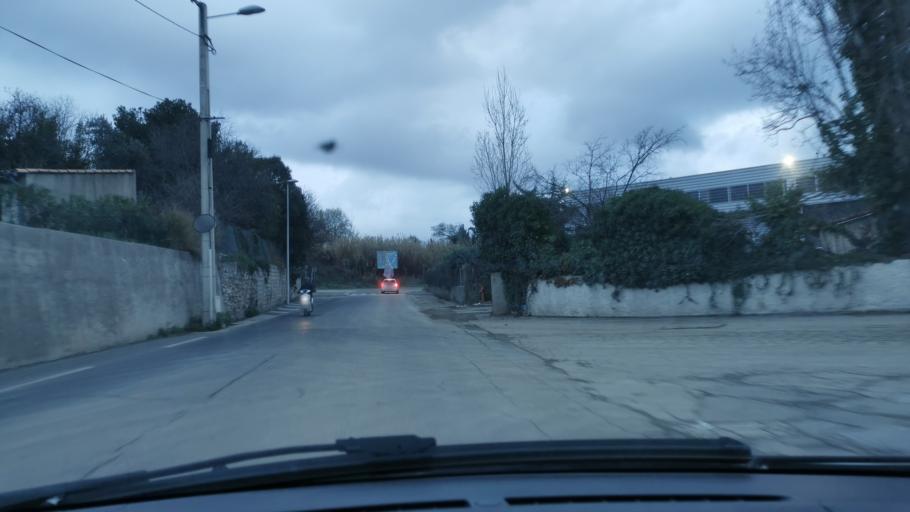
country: FR
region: Languedoc-Roussillon
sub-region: Departement de l'Herault
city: Montpellier
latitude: 43.5844
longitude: 3.8695
